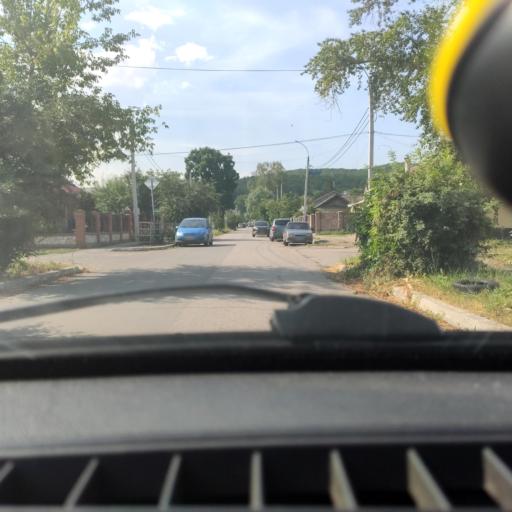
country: RU
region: Samara
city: Zhigulevsk
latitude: 53.4050
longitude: 49.4832
